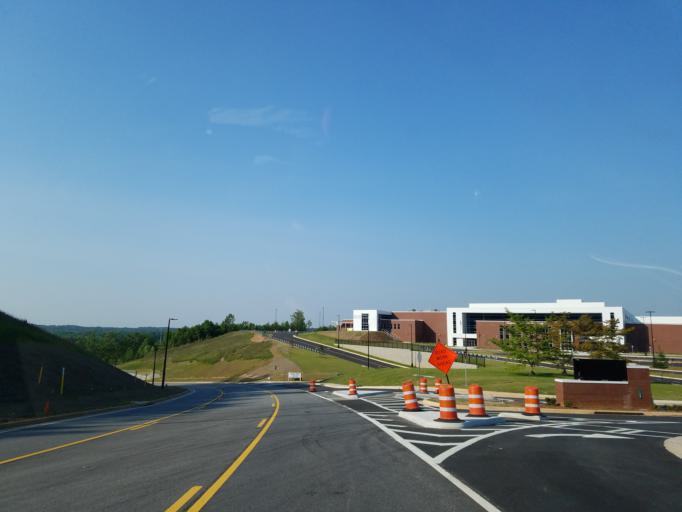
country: US
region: Georgia
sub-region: Forsyth County
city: Cumming
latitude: 34.2174
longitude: -84.1175
